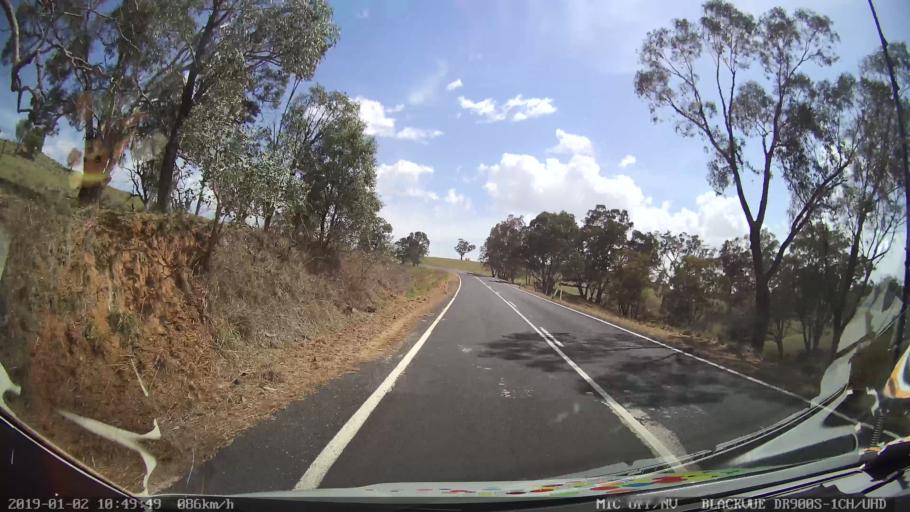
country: AU
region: New South Wales
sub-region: Cootamundra
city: Cootamundra
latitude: -34.7198
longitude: 148.2766
